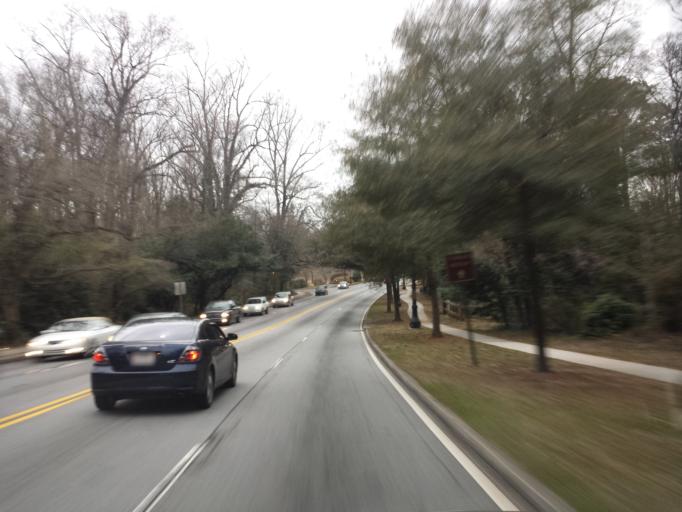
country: US
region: Georgia
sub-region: DeKalb County
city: Druid Hills
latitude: 33.7718
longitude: -84.3257
